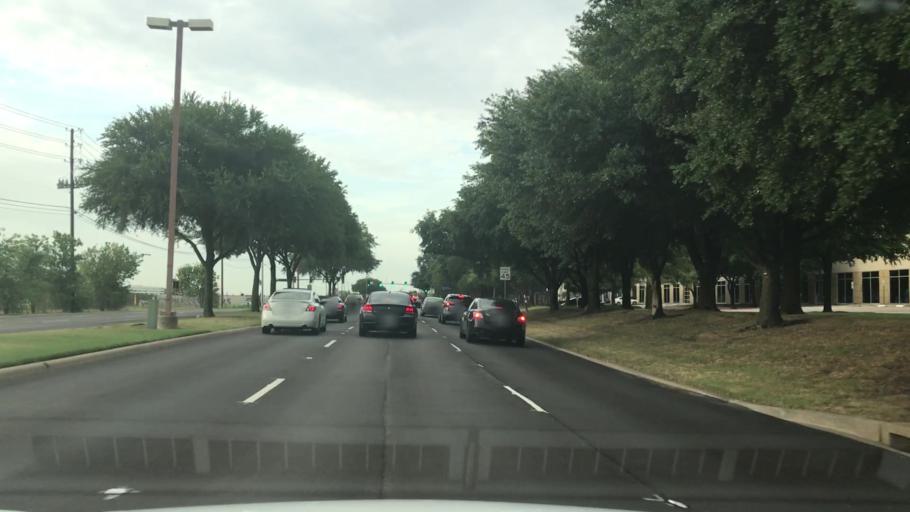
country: US
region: Texas
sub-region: Dallas County
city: Coppell
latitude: 32.9418
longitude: -96.9936
